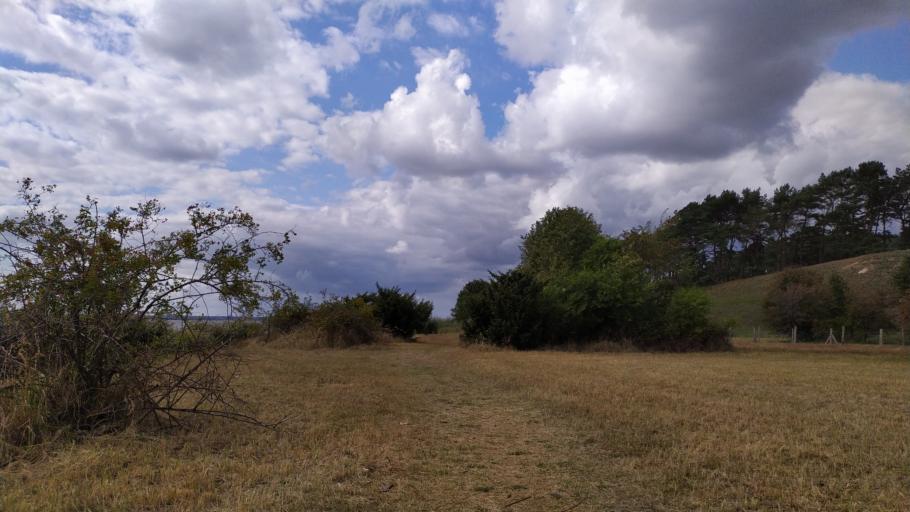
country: DE
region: Mecklenburg-Vorpommern
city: Lassan
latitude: 54.0010
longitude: 13.8586
